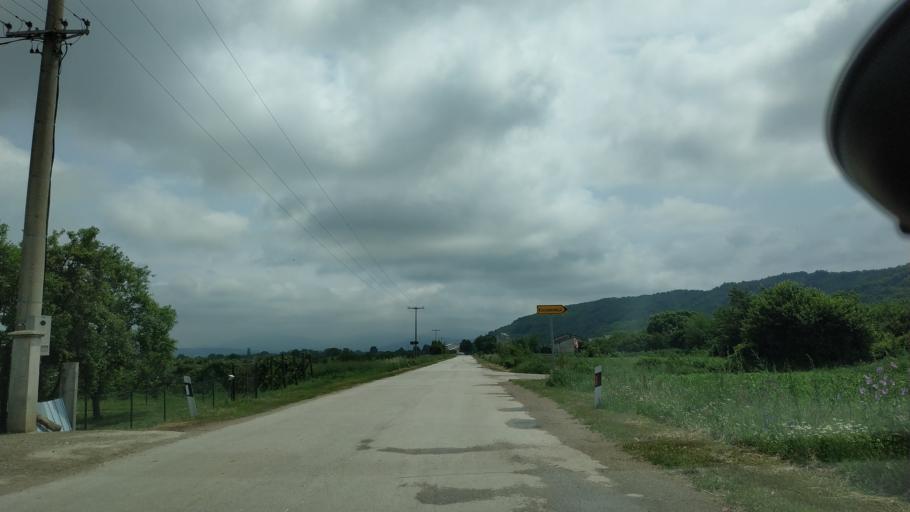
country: RS
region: Central Serbia
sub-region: Nisavski Okrug
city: Aleksinac
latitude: 43.4392
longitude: 21.7186
